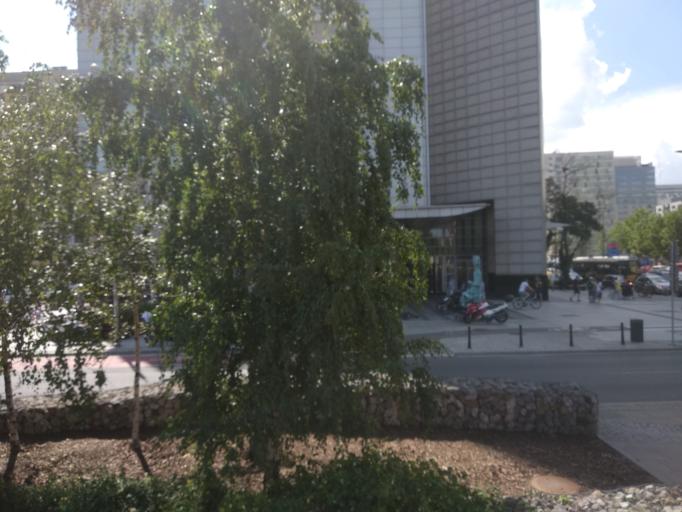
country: PL
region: Masovian Voivodeship
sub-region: Warszawa
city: Warsaw
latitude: 52.2336
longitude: 21.0025
